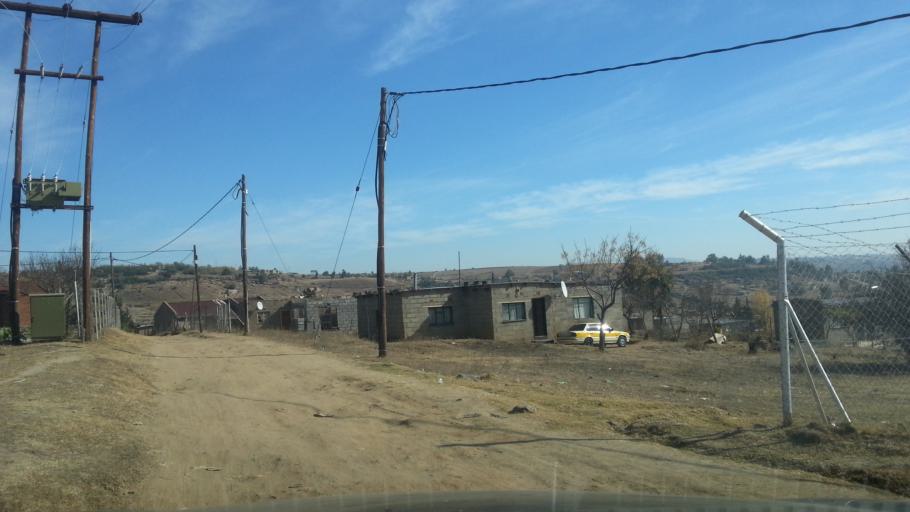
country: LS
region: Maseru
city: Maseru
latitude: -29.4182
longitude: 27.5534
